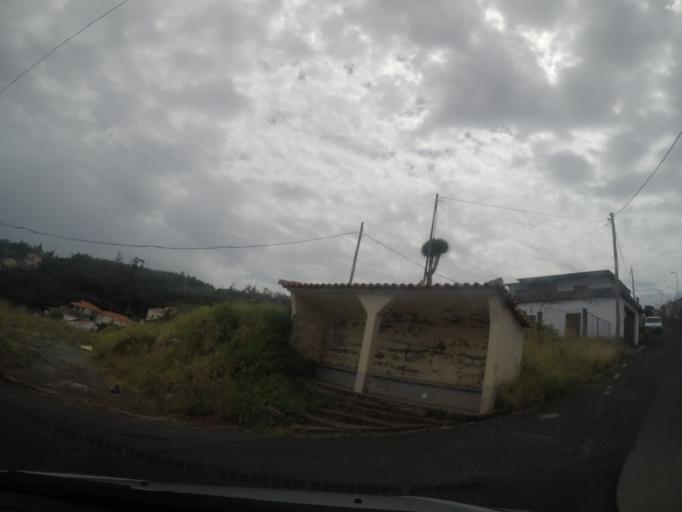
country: PT
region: Madeira
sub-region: Santa Cruz
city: Santa Cruz
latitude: 32.6891
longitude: -16.8128
